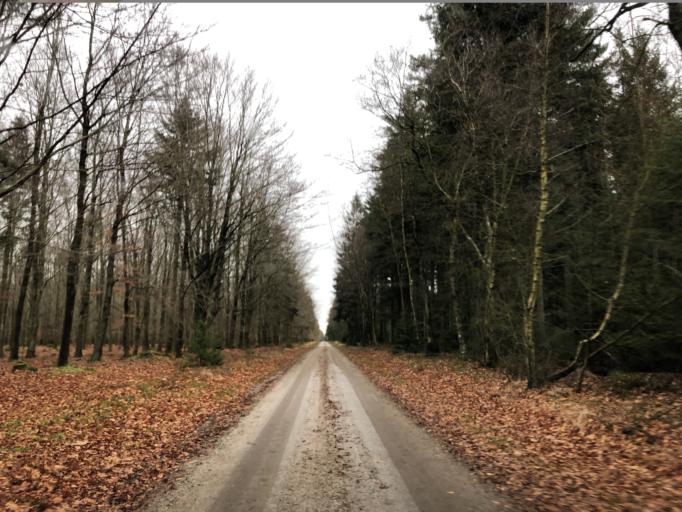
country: DK
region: Central Jutland
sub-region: Holstebro Kommune
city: Vinderup
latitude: 56.3837
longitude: 8.8665
